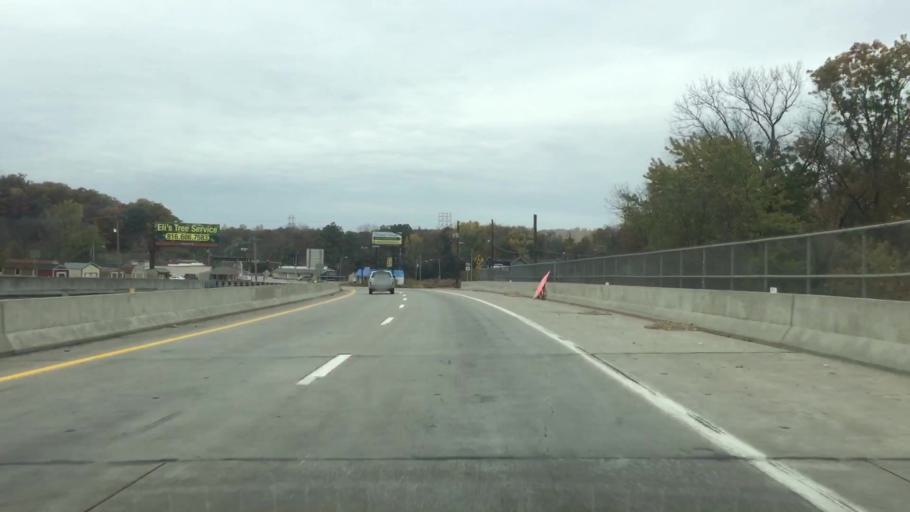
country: US
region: Missouri
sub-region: Jackson County
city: Raytown
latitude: 38.9639
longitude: -94.4264
